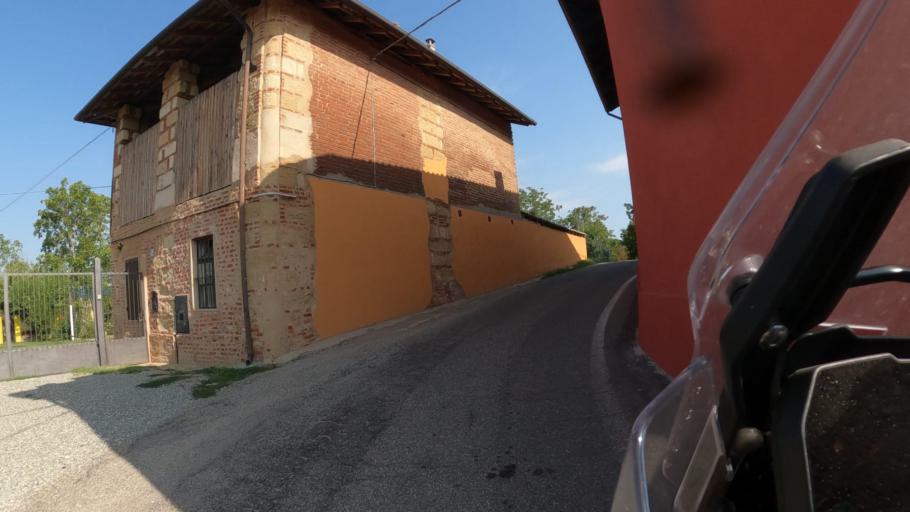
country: IT
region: Piedmont
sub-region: Provincia di Asti
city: Viarigi
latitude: 44.9548
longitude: 8.3734
